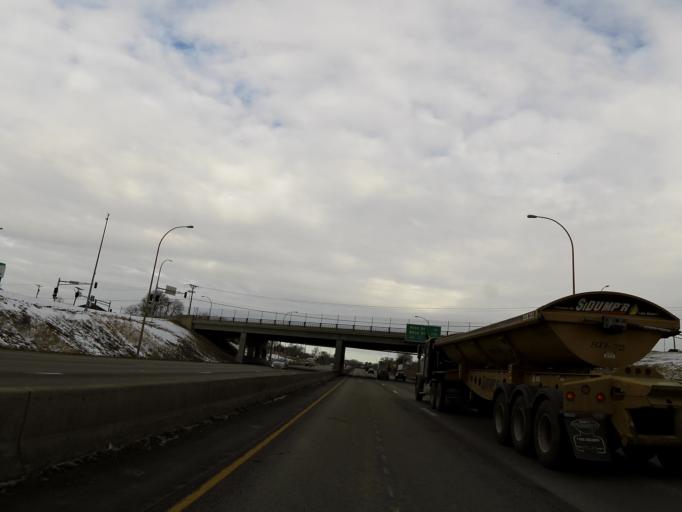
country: US
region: Minnesota
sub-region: Hennepin County
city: Bloomington
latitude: 44.8328
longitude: -93.2945
